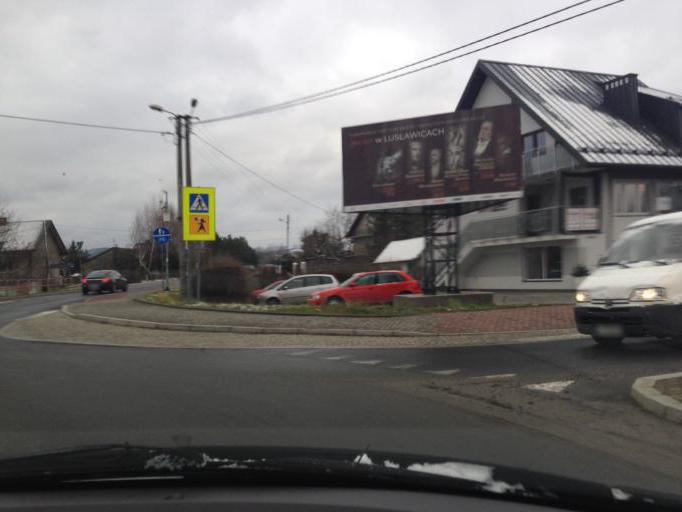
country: PL
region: Lesser Poland Voivodeship
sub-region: Powiat tarnowski
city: Zakliczyn
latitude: 49.8563
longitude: 20.8136
